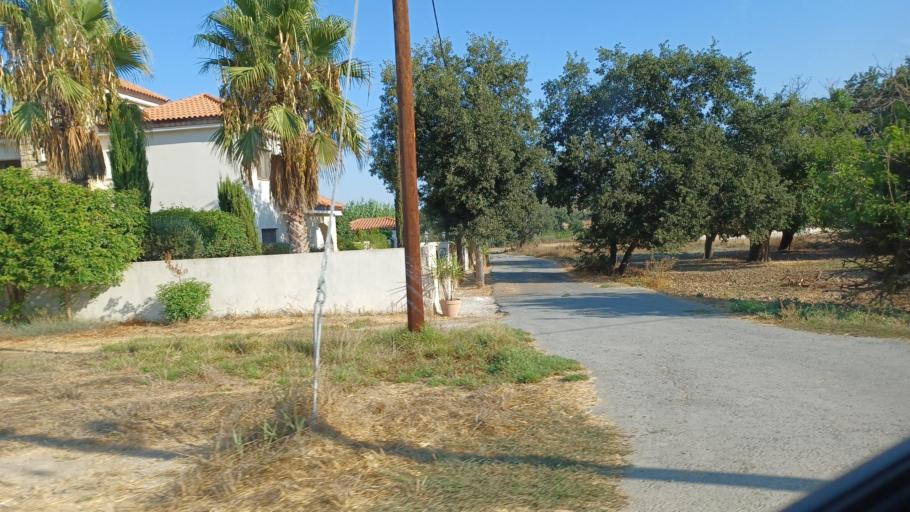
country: CY
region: Pafos
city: Mesogi
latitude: 34.8900
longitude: 32.5104
